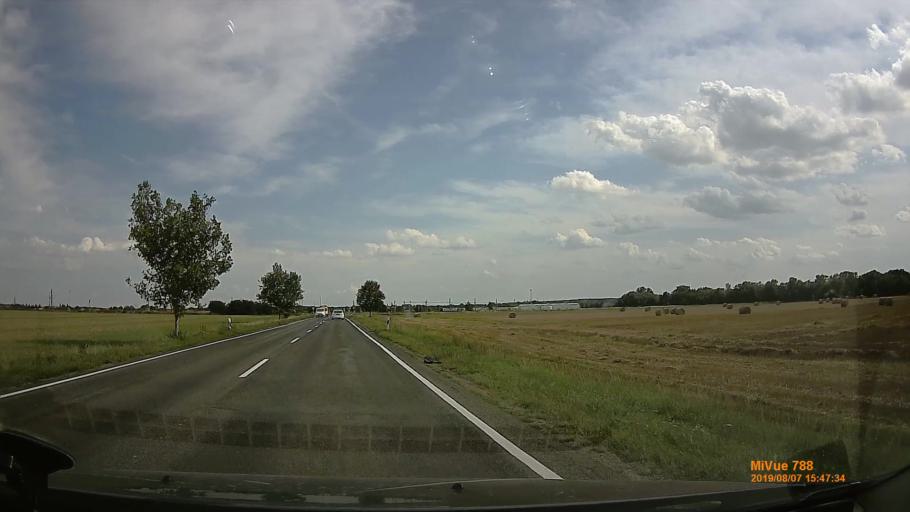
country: HU
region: Vas
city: Jak
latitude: 47.1697
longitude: 16.6287
